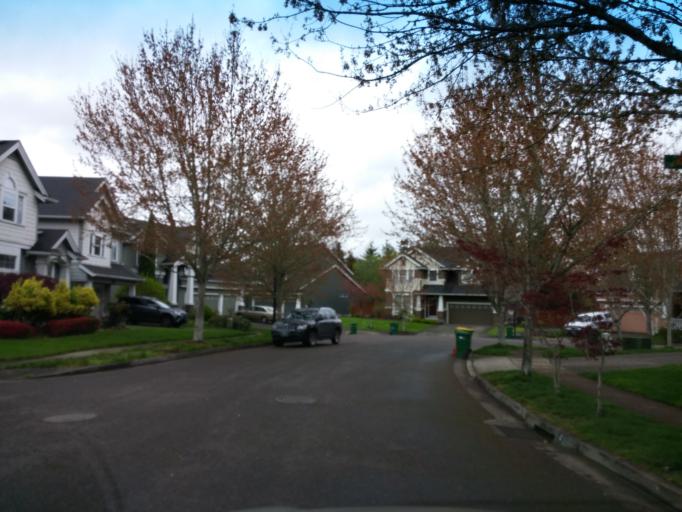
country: US
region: Oregon
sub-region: Washington County
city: Oak Hills
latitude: 45.5192
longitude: -122.8494
